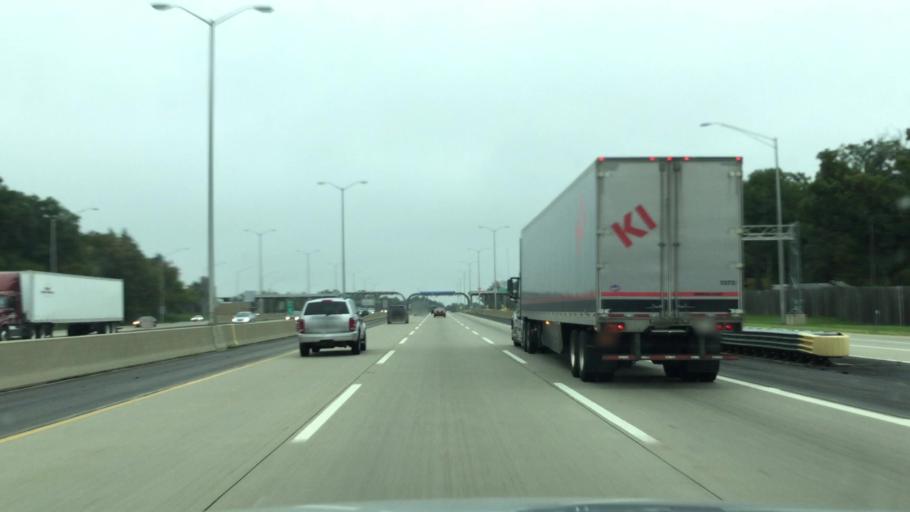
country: US
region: Illinois
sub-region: Lake County
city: Wadsworth
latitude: 42.4296
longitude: -87.9498
